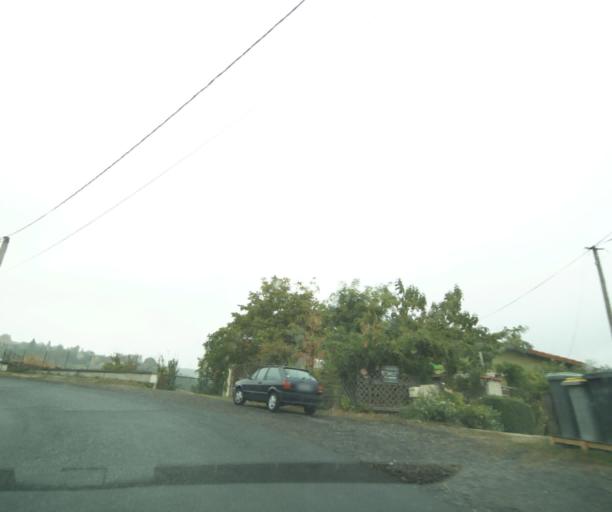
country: FR
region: Auvergne
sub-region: Departement du Puy-de-Dome
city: Chateaugay
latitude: 45.8484
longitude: 3.0928
